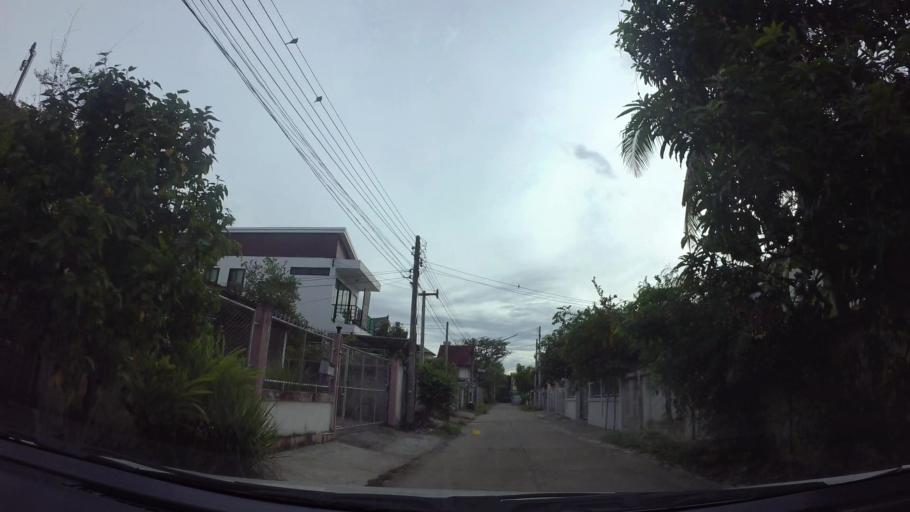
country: TH
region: Chiang Mai
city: Chiang Mai
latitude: 18.7605
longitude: 98.9809
